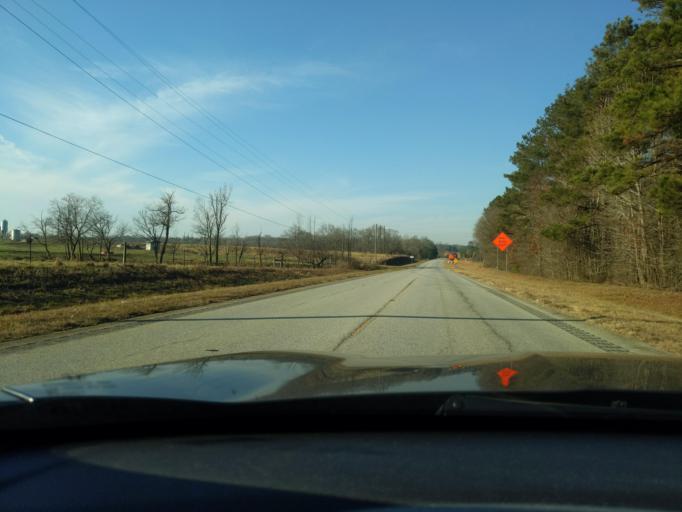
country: US
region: South Carolina
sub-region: Newberry County
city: Newberry
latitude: 34.2117
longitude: -81.7594
